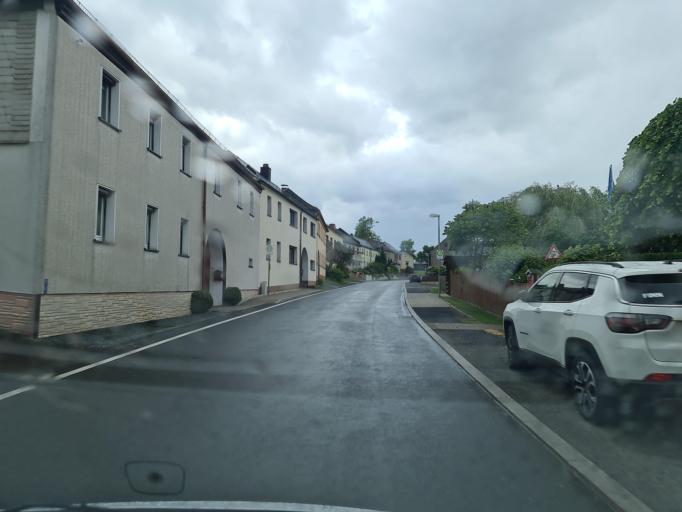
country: DE
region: Saxony
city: Reuth
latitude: 50.4865
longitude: 11.9450
